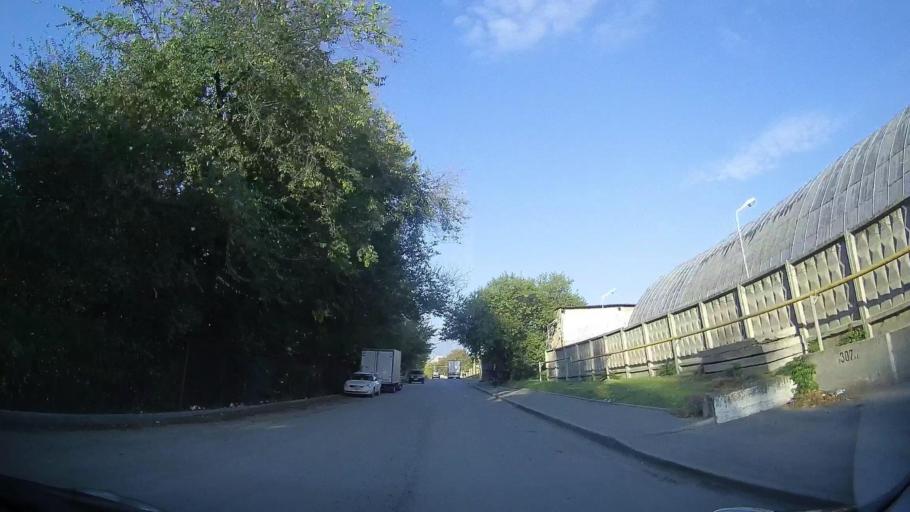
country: RU
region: Rostov
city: Severnyy
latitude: 47.2720
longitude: 39.6826
